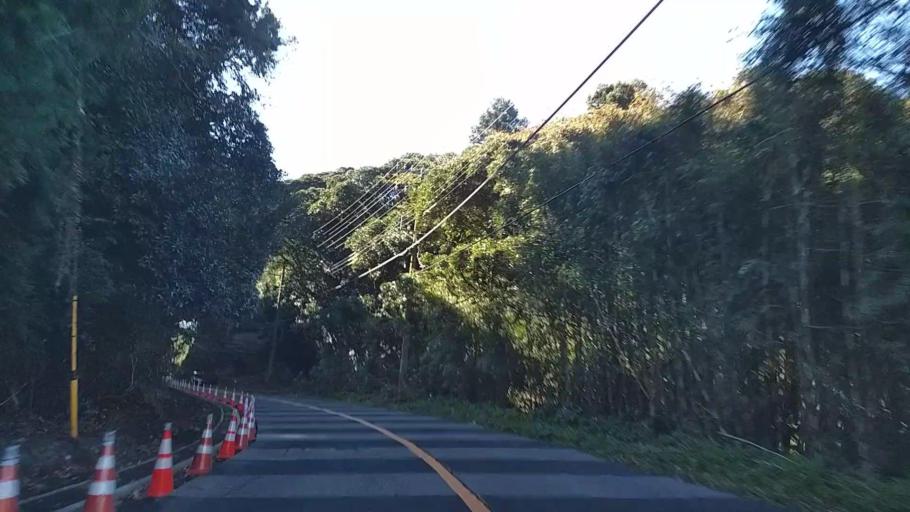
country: JP
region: Chiba
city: Tateyama
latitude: 34.9623
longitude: 139.8553
